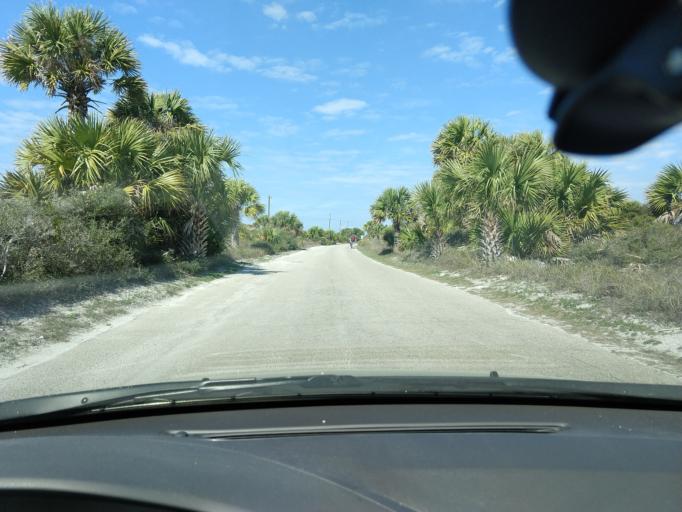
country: US
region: Florida
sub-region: Gulf County
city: Port Saint Joe
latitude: 29.7721
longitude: -85.4057
